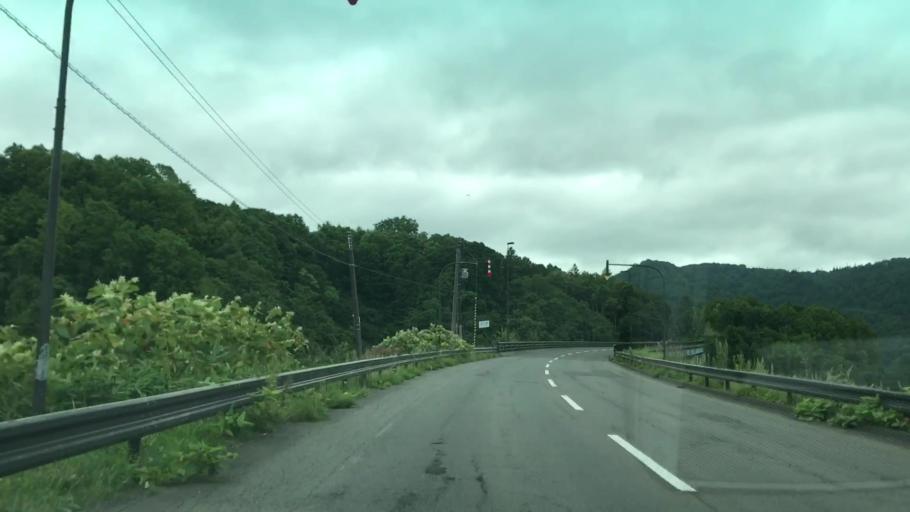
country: JP
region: Hokkaido
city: Otaru
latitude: 42.9968
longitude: 140.8791
